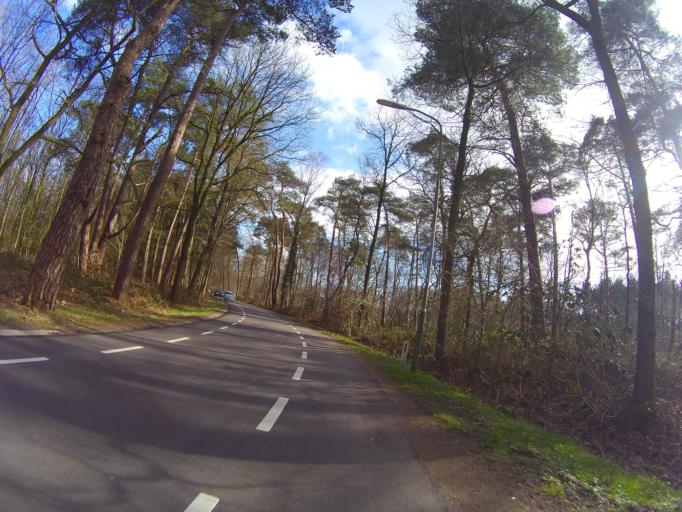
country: NL
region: Gelderland
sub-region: Gemeente Barneveld
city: Terschuur
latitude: 52.1469
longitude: 5.5466
